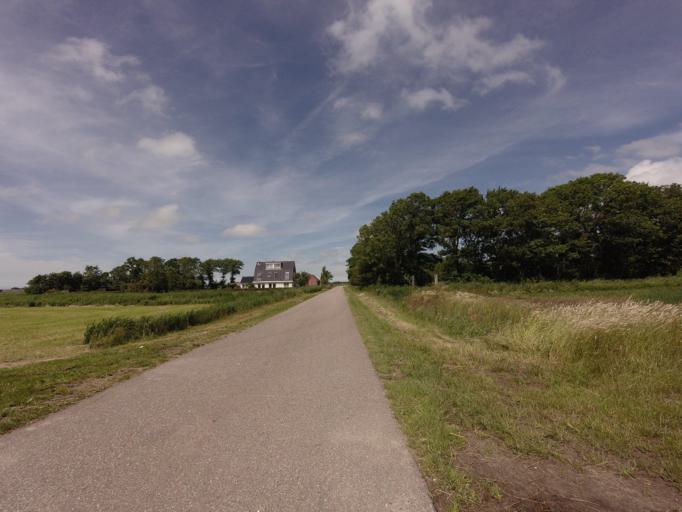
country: NL
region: North Holland
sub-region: Gemeente Texel
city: Den Burg
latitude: 53.0754
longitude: 4.8828
